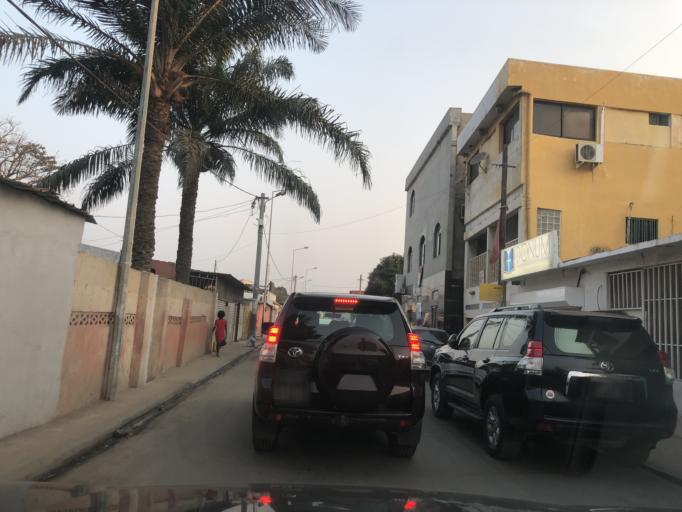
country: AO
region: Luanda
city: Luanda
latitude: -8.8442
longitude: 13.2248
